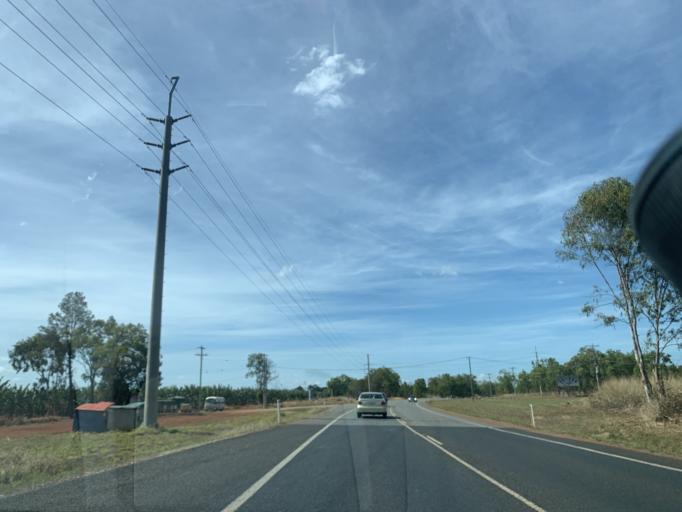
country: AU
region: Queensland
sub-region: Tablelands
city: Mareeba
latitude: -17.0857
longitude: 145.4351
